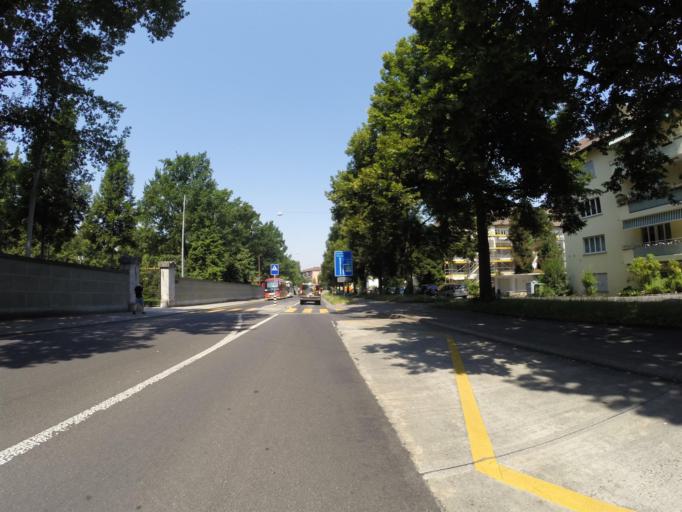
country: CH
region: Bern
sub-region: Bern-Mittelland District
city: Bern
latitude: 46.9523
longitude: 7.4612
